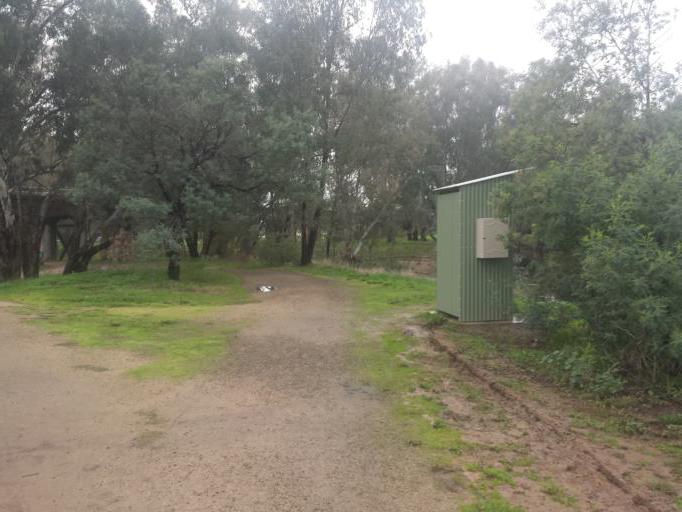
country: AU
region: Victoria
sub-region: Benalla
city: Benalla
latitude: -36.5481
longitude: 145.9757
